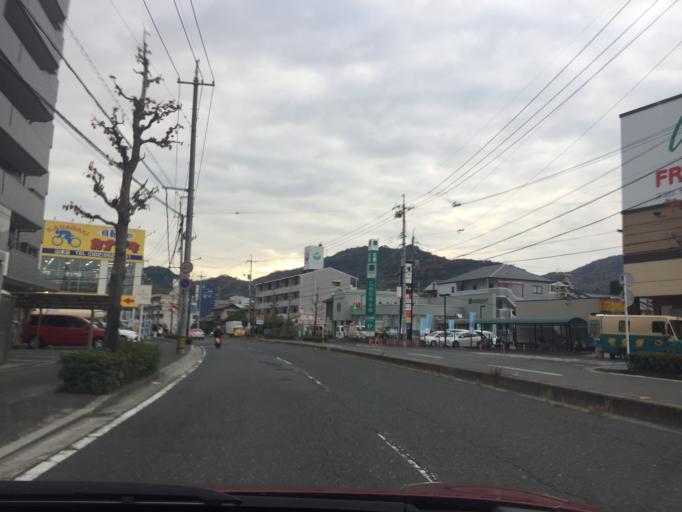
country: JP
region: Hiroshima
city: Hiroshima-shi
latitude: 34.4383
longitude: 132.4555
